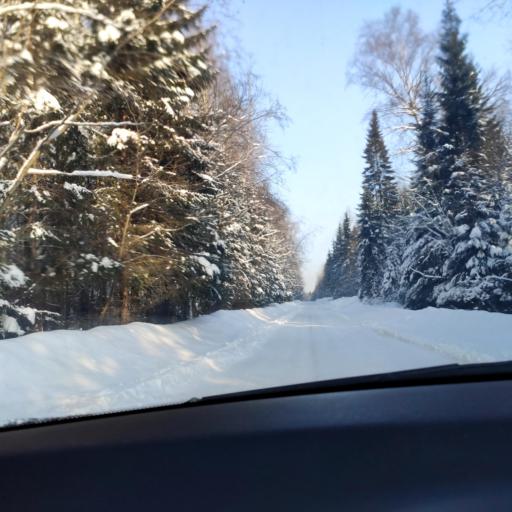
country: RU
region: Perm
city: Kondratovo
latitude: 58.0767
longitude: 56.1297
